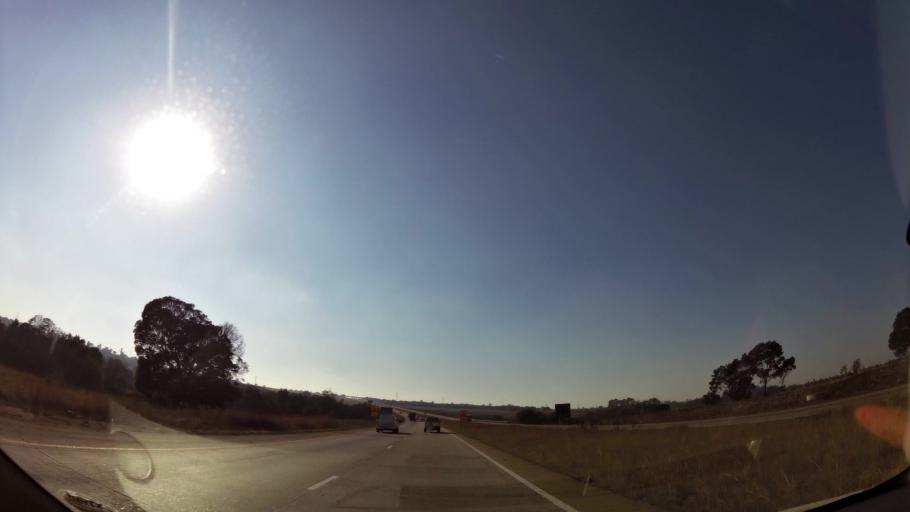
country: ZA
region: Mpumalanga
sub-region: Nkangala District Municipality
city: Witbank
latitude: -26.0225
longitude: 29.0501
